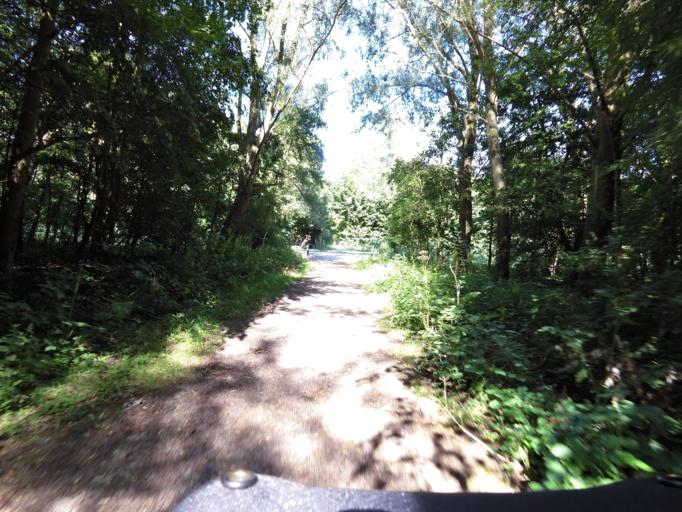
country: NL
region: South Holland
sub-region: Gemeente Goeree-Overflakkee
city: Goedereede
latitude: 51.8054
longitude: 4.0168
